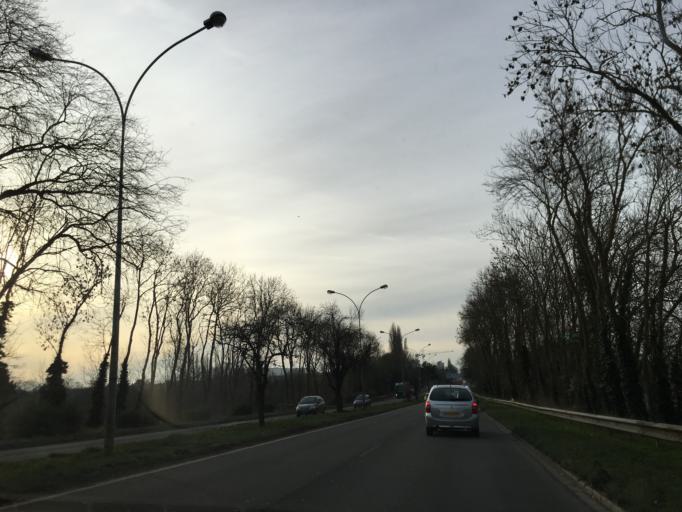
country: FR
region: Nord-Pas-de-Calais
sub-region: Departement du Pas-de-Calais
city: Saint-Nicolas
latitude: 50.3012
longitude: 2.7839
